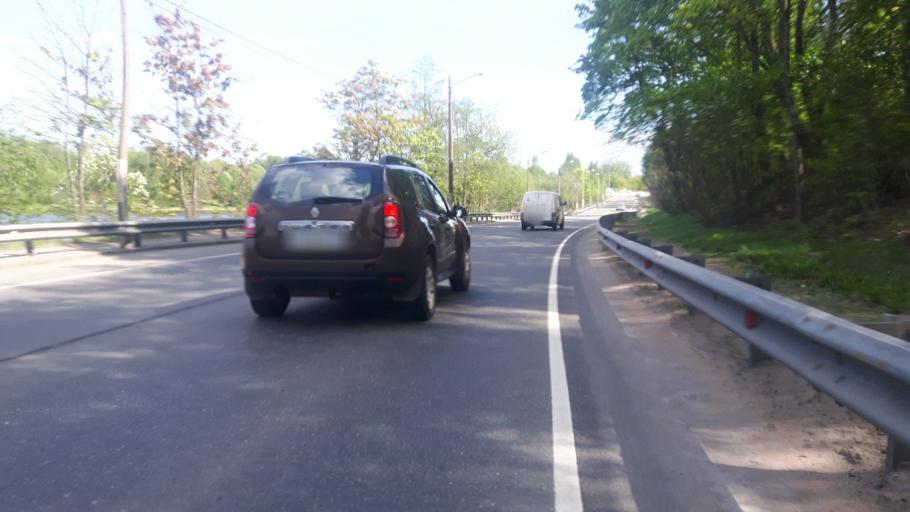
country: RU
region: Leningrad
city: Vyborg
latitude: 60.7239
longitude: 28.7117
